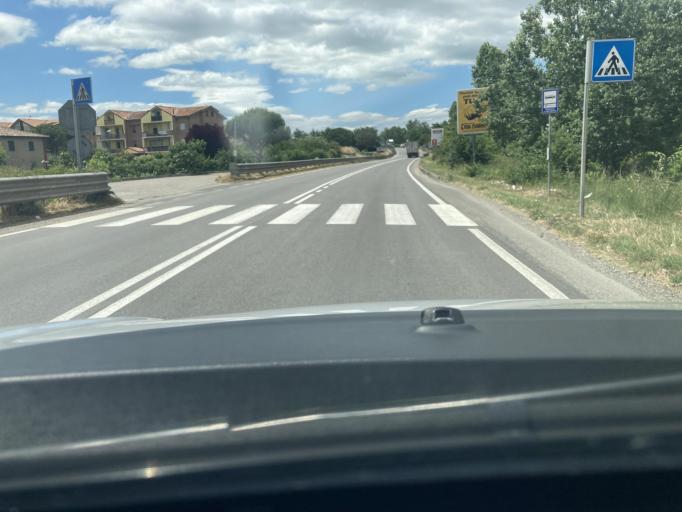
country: IT
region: Umbria
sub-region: Provincia di Perugia
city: Corciano
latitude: 43.1331
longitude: 12.2586
